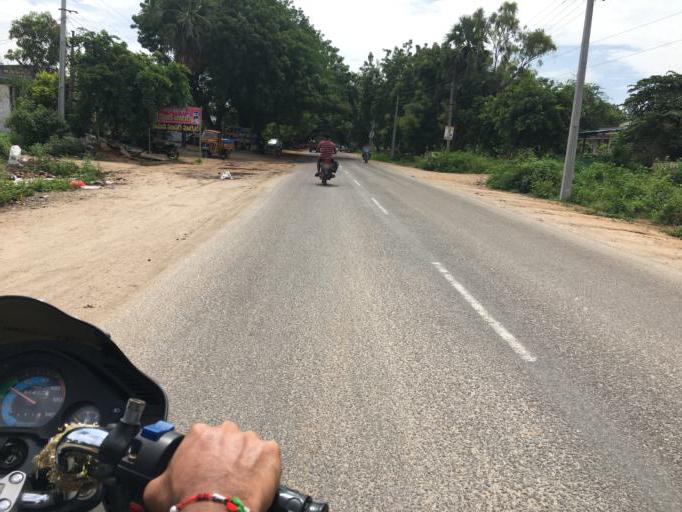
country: IN
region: Telangana
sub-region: Nalgonda
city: Nalgonda
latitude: 17.1672
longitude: 79.4135
